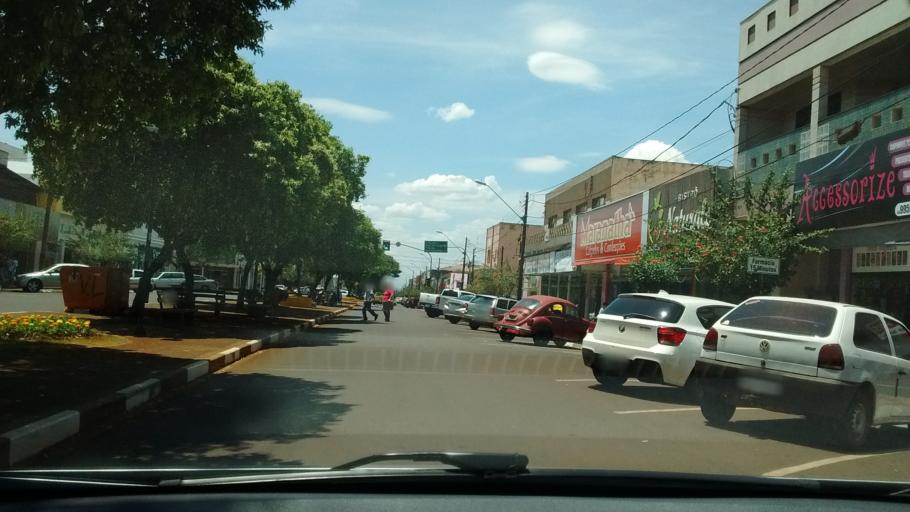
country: BR
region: Parana
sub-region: Corbelia
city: Corbelia
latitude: -24.5436
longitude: -52.9898
